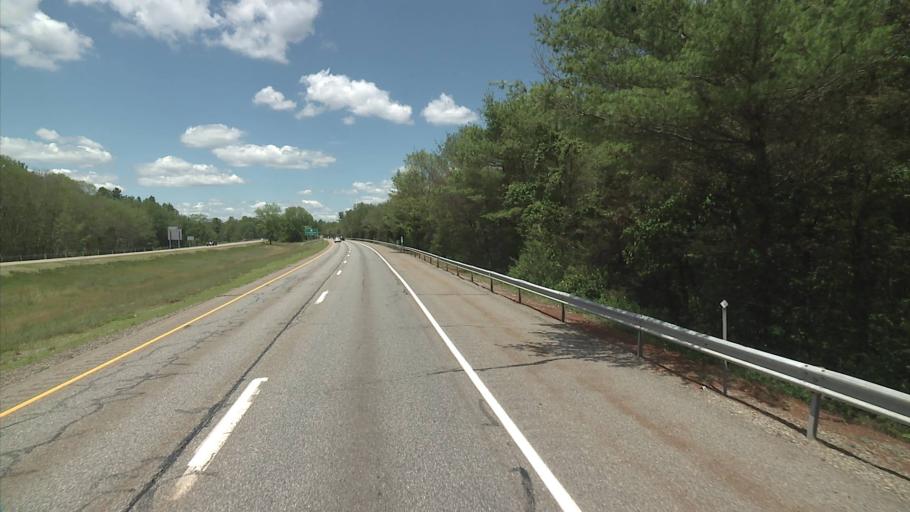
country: US
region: Connecticut
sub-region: Windham County
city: Thompson
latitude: 41.9402
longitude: -71.8779
